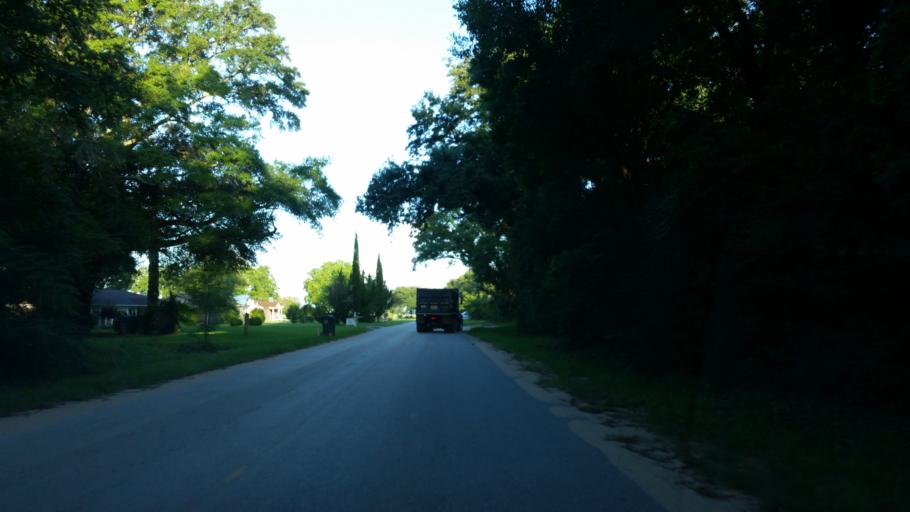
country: US
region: Florida
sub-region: Escambia County
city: Bellview
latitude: 30.4691
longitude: -87.3300
